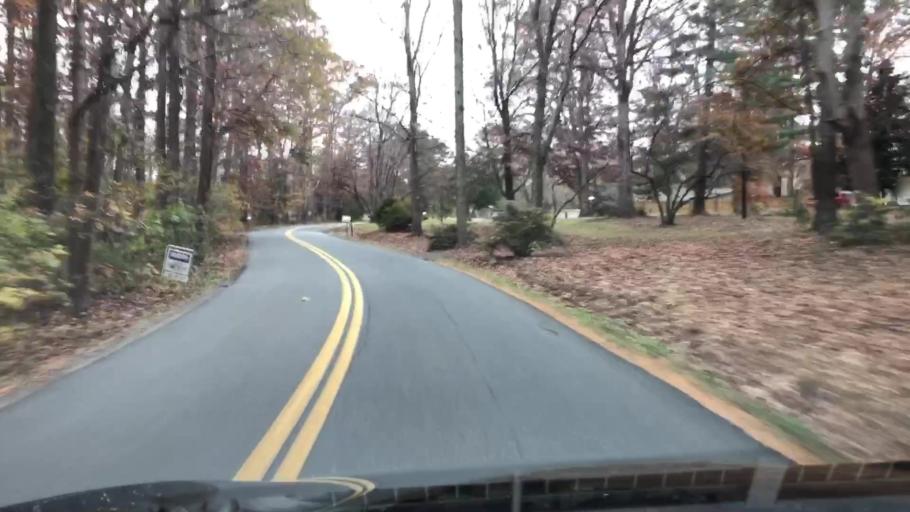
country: US
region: Virginia
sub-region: Stafford County
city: Falmouth
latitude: 38.3889
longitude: -77.5866
